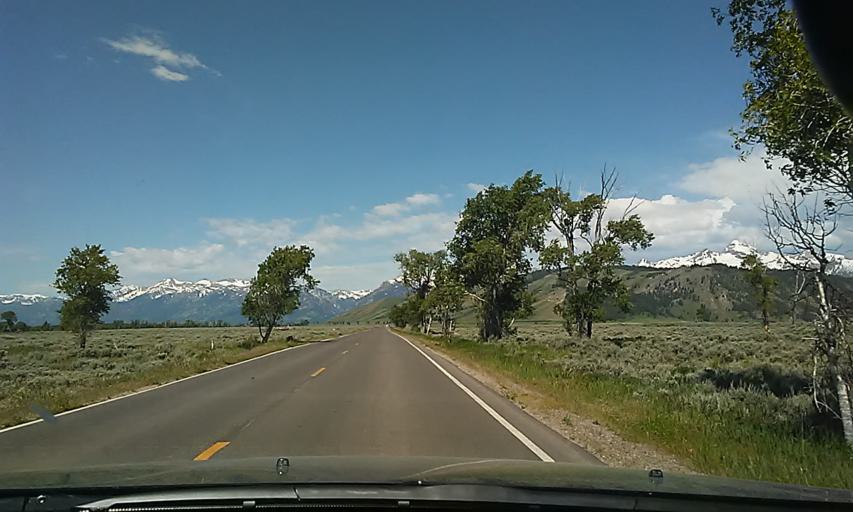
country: US
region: Wyoming
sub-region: Teton County
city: Jackson
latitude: 43.6251
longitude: -110.6352
